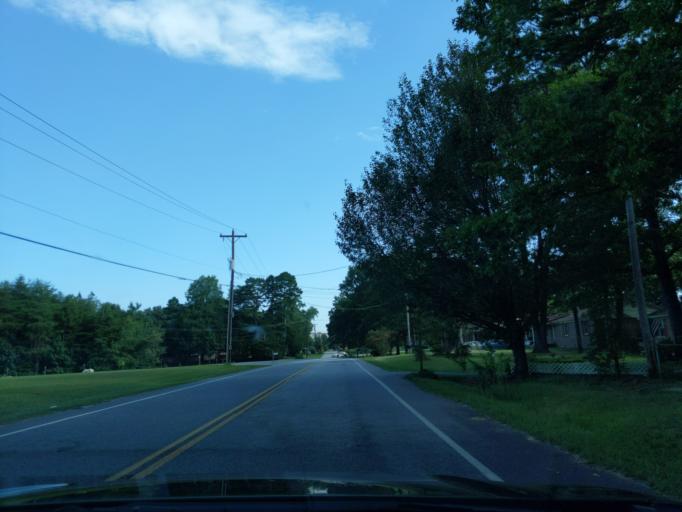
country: US
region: South Carolina
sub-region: Greenville County
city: Mauldin
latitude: 34.8163
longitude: -82.3116
